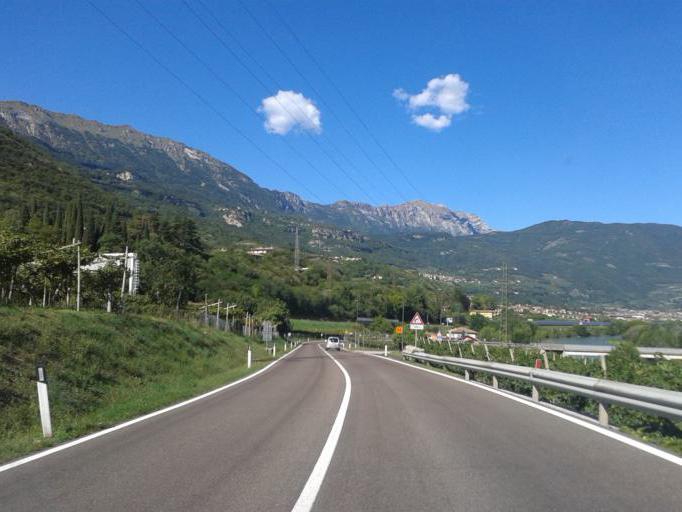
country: IT
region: Trentino-Alto Adige
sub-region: Provincia di Trento
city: Isera
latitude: 45.8865
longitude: 11.0137
